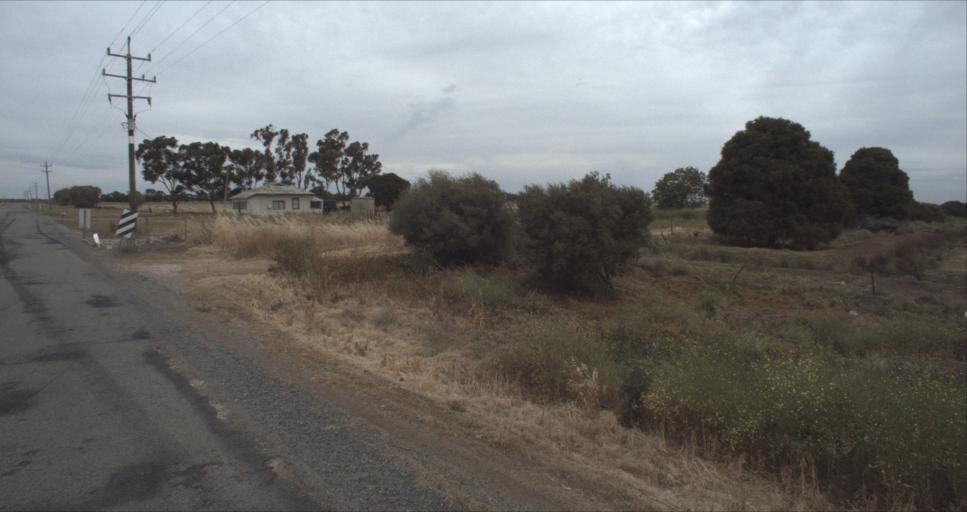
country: AU
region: New South Wales
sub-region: Leeton
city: Leeton
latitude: -34.4943
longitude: 146.4009
